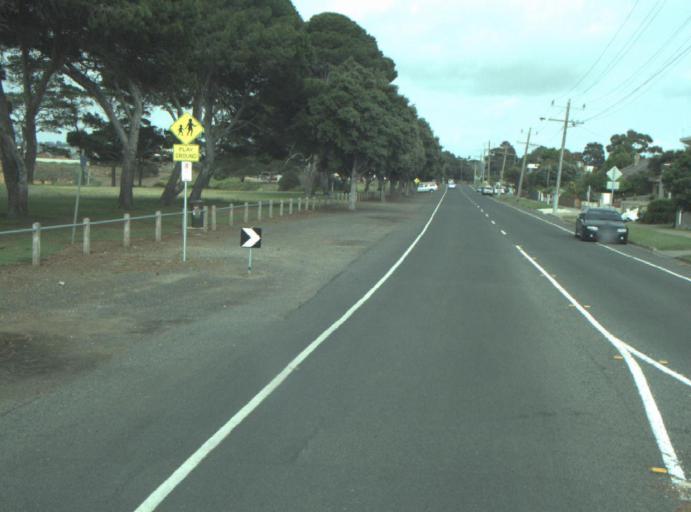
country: AU
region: Victoria
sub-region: Greater Geelong
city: Bell Park
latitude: -38.1008
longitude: 144.3756
